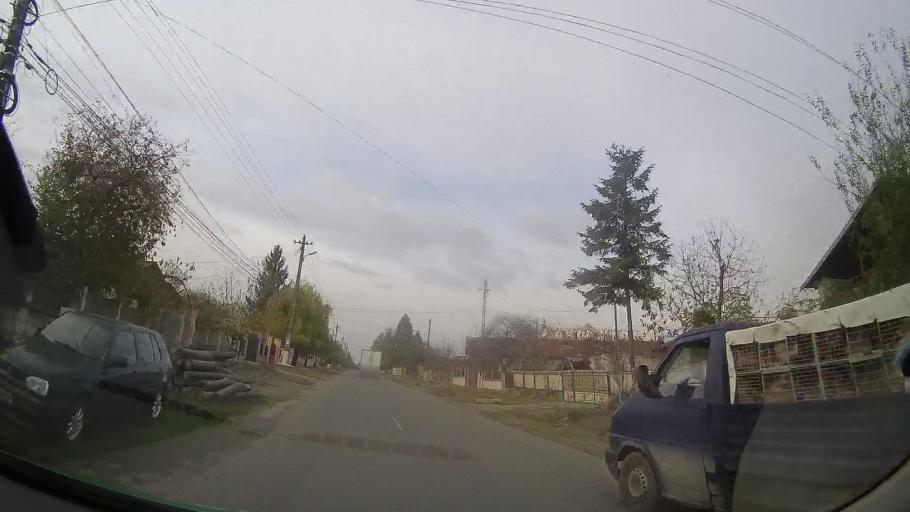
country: RO
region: Prahova
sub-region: Comuna Gorgota
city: Potigrafu
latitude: 44.7742
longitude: 26.1066
